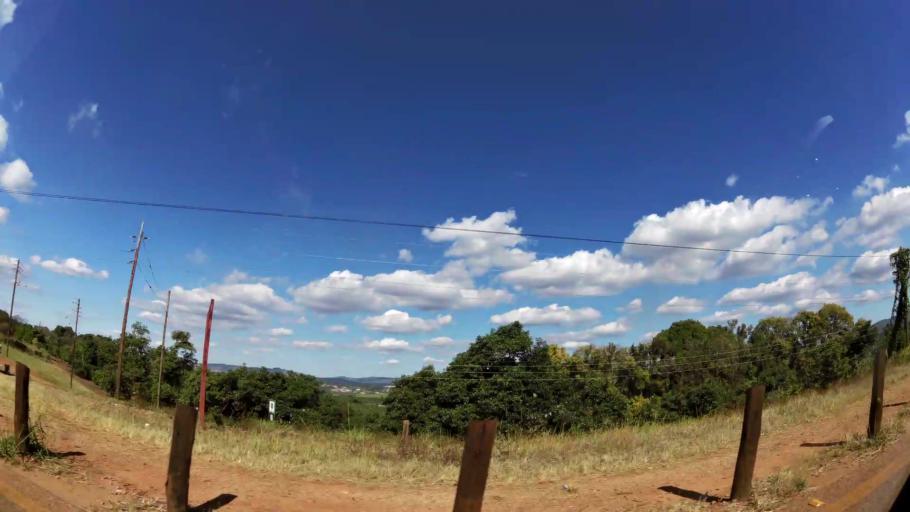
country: ZA
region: Limpopo
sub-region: Mopani District Municipality
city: Tzaneen
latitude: -23.8025
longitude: 30.1228
